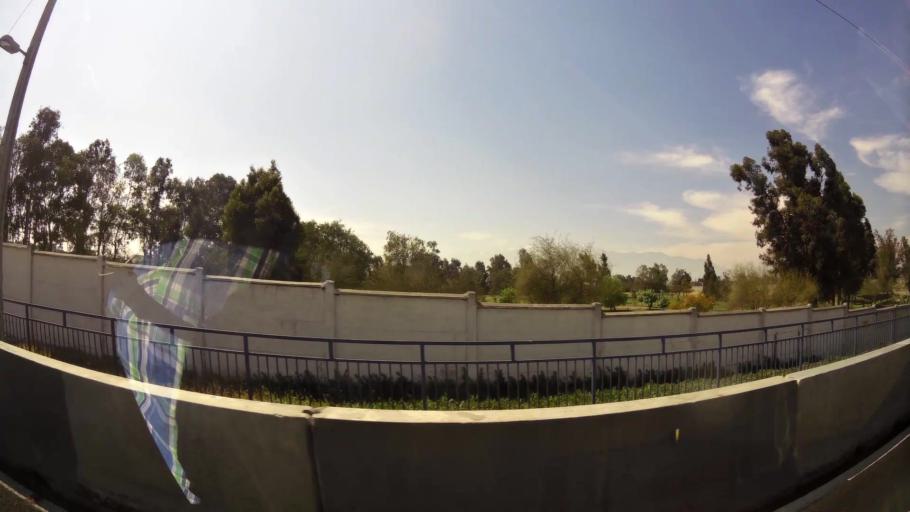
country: CL
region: Santiago Metropolitan
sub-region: Provincia de Santiago
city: Lo Prado
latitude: -33.4763
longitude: -70.7028
